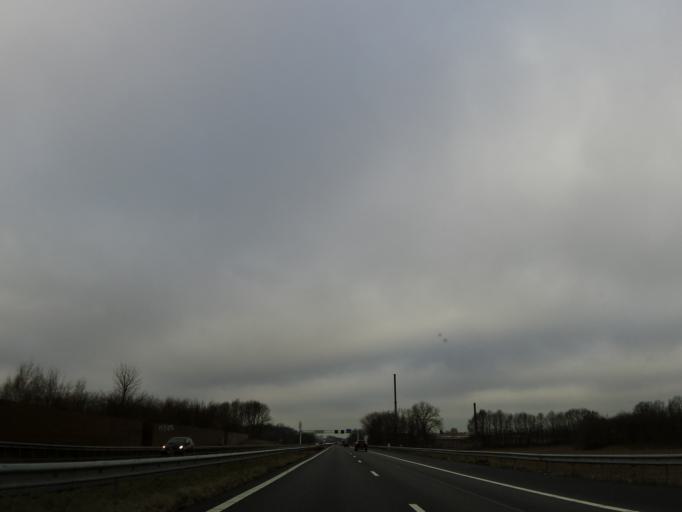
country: NL
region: Limburg
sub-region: Gemeente Maasgouw
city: Maasbracht
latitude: 51.1679
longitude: 5.8765
